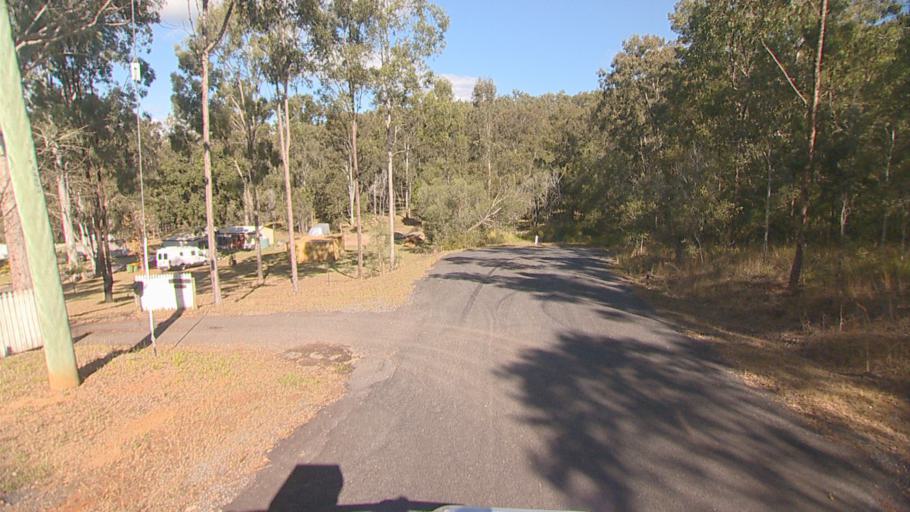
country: AU
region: Queensland
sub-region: Logan
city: Chambers Flat
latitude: -27.8137
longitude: 153.0890
